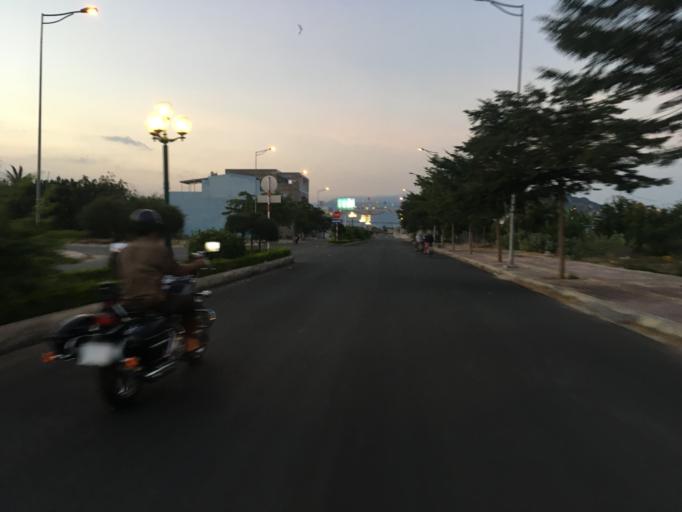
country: VN
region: Ninh Thuan
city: Phan Rang-Thap Cham
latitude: 11.5760
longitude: 109.0012
